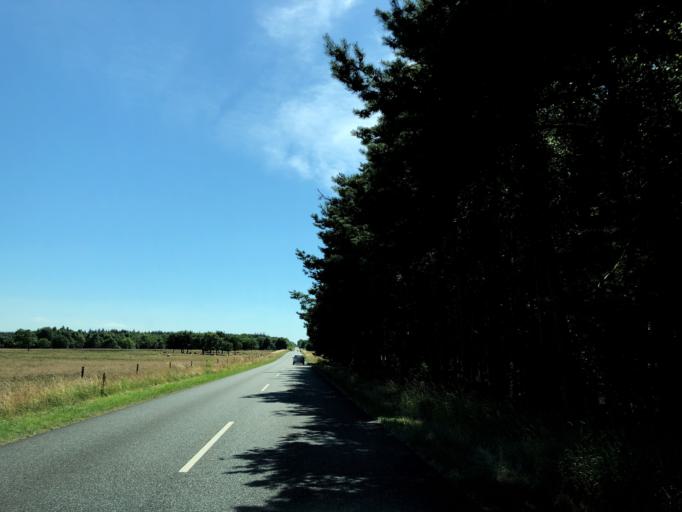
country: DK
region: Central Jutland
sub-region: Skive Kommune
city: Skive
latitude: 56.5282
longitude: 9.0348
